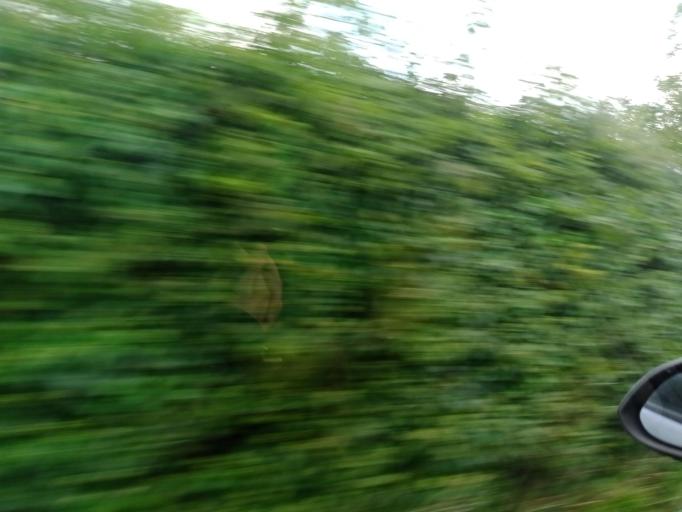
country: IE
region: Leinster
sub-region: Uibh Fhaili
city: Tullamore
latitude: 53.1441
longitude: -7.4628
